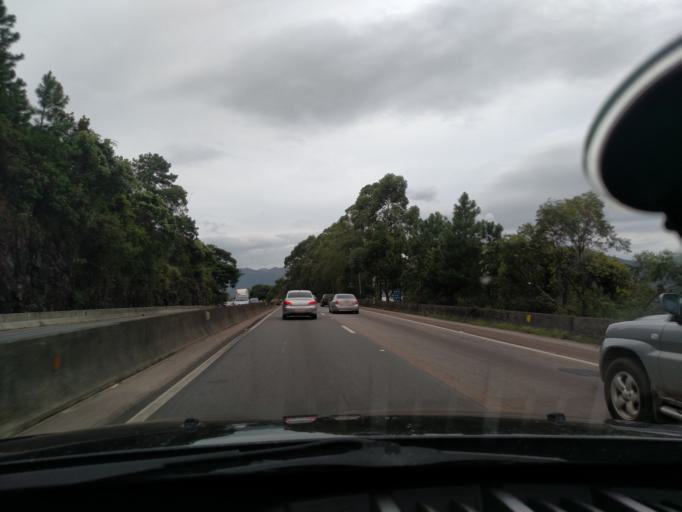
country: BR
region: Santa Catarina
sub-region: Biguacu
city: Biguacu
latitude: -27.4436
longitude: -48.6287
